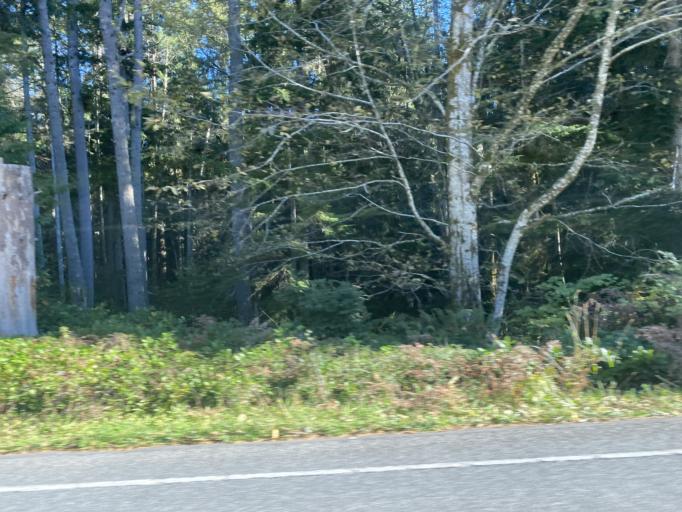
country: US
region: Washington
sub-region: Island County
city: Langley
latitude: 48.0201
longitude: -122.4270
